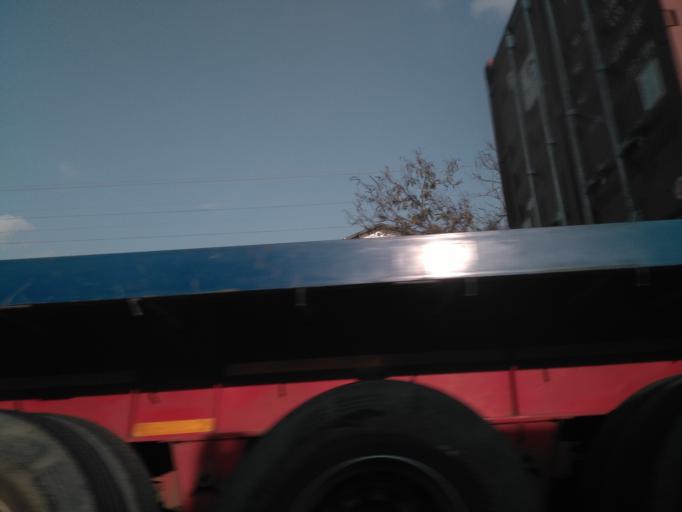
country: TZ
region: Dar es Salaam
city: Magomeni
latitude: -6.7528
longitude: 39.2345
